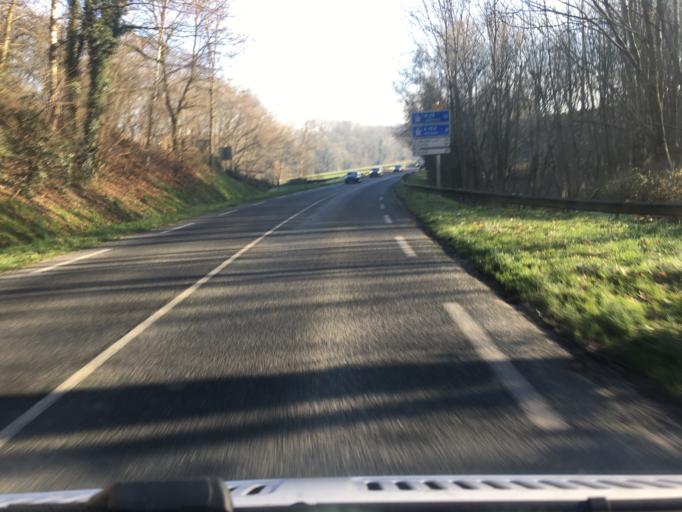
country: FR
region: Haute-Normandie
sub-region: Departement de la Seine-Maritime
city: Yvetot
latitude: 49.6068
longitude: 0.7448
